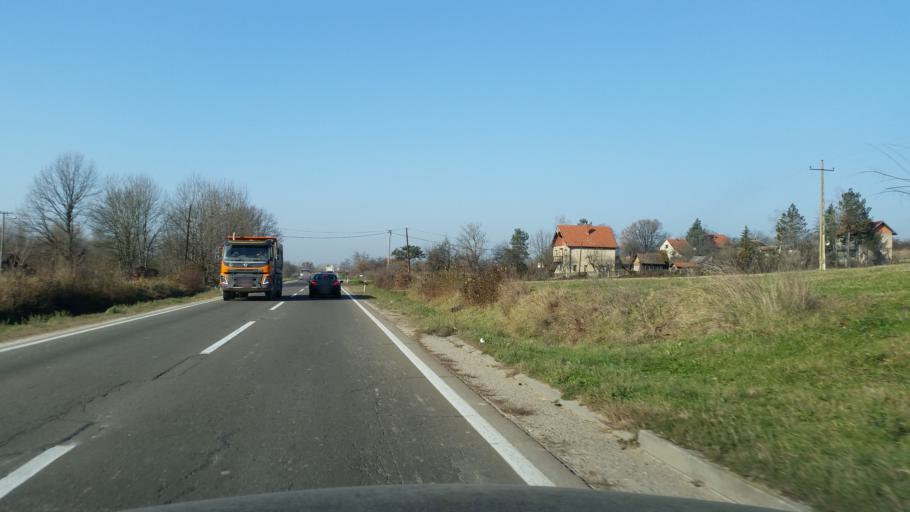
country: RS
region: Central Serbia
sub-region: Kolubarski Okrug
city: Ljig
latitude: 44.2882
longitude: 20.2697
